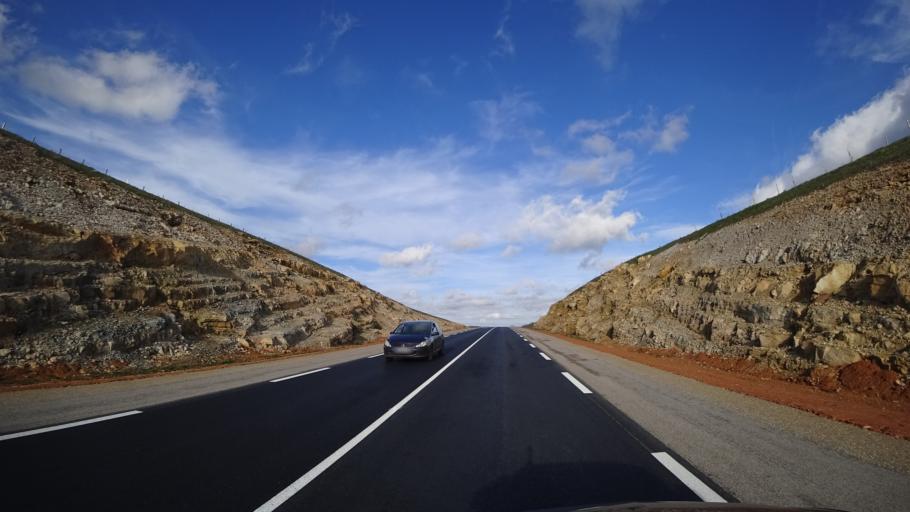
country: FR
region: Midi-Pyrenees
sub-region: Departement de l'Aveyron
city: Sebazac-Concoures
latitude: 44.4022
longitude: 2.6201
